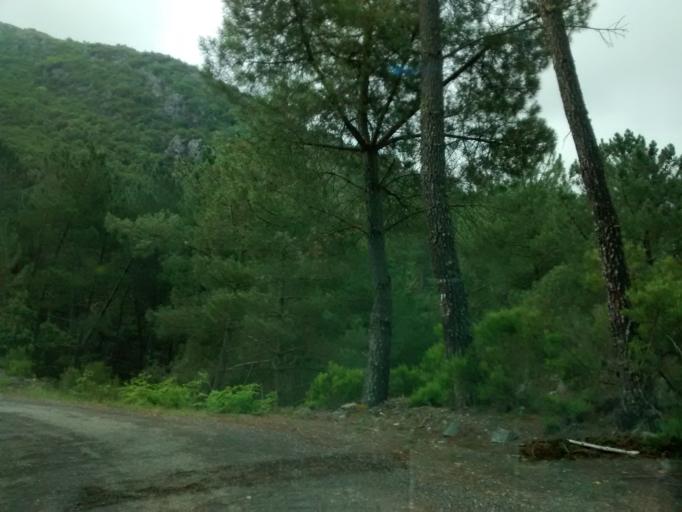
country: ES
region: Galicia
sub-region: Provincia de Ourense
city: Castro Caldelas
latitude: 42.4194
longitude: -7.3868
